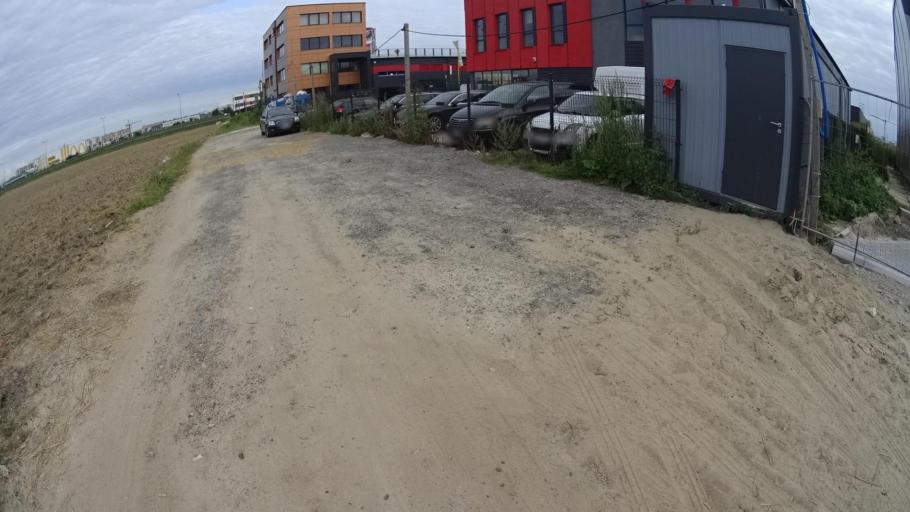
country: PL
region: Masovian Voivodeship
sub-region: Warszawa
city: Bemowo
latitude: 52.2350
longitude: 20.8811
